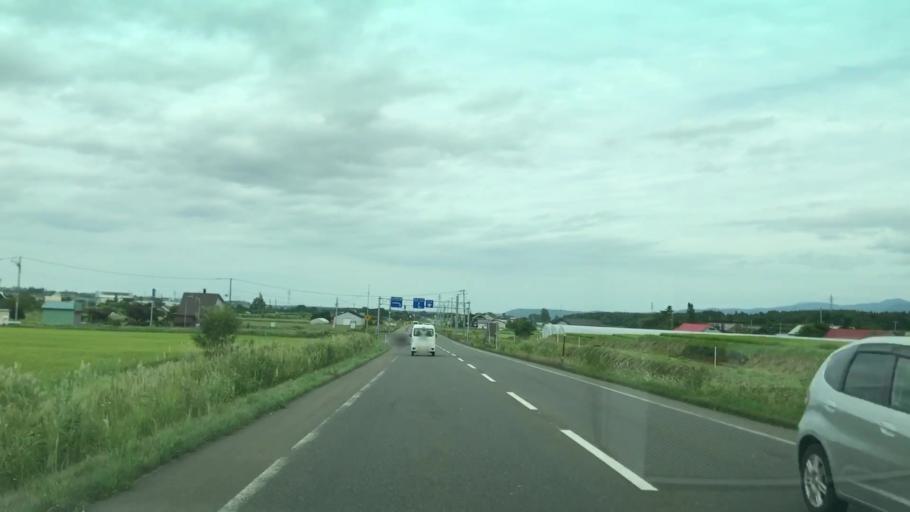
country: JP
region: Hokkaido
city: Iwanai
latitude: 42.9799
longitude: 140.6245
